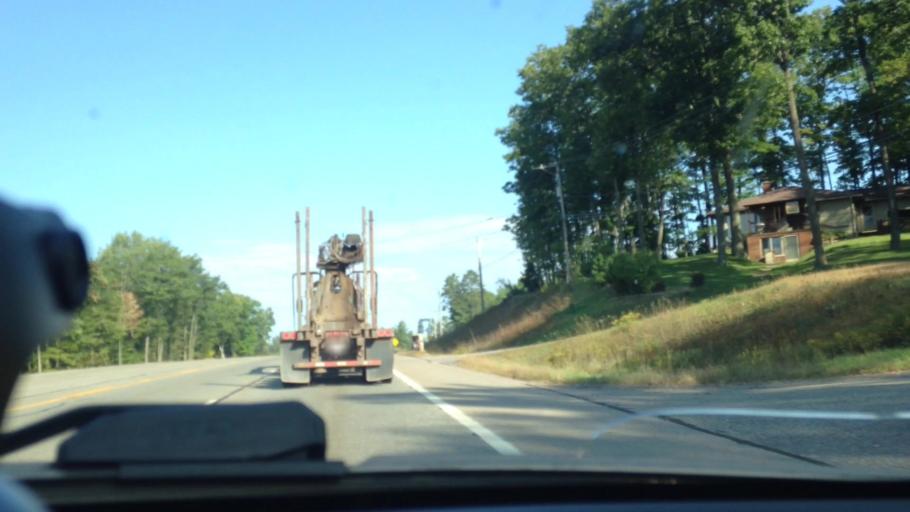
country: US
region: Michigan
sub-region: Dickinson County
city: Iron Mountain
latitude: 45.8562
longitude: -88.0577
